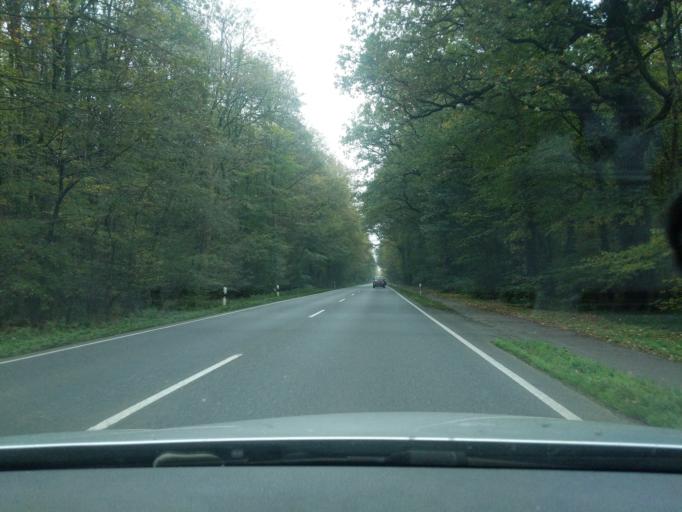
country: DE
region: Lower Saxony
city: Himmelpforten
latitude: 53.6023
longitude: 9.3206
